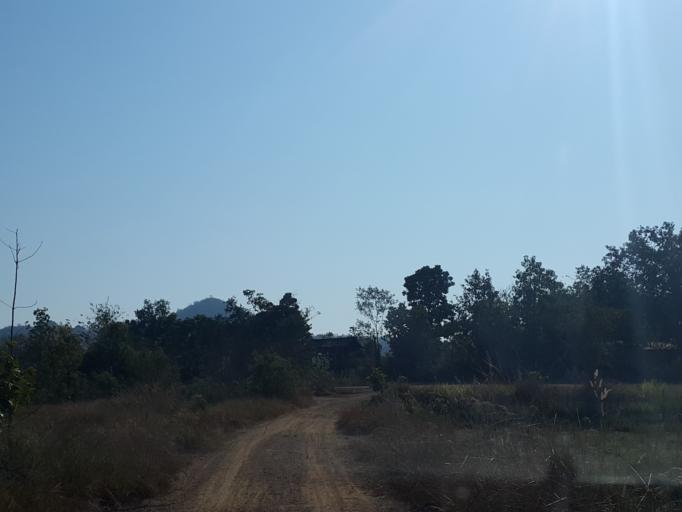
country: TH
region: Sukhothai
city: Thung Saliam
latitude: 17.3123
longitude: 99.4343
